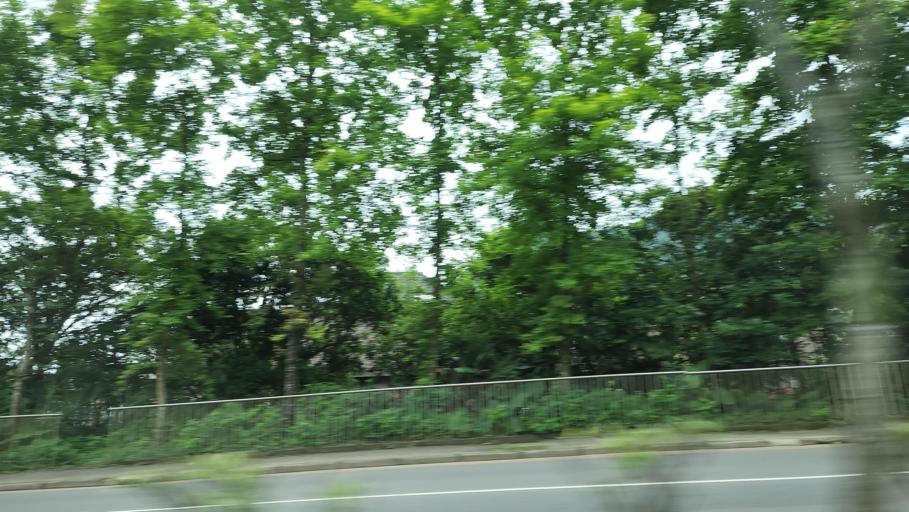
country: TW
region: Taiwan
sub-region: Keelung
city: Keelung
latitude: 25.1612
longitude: 121.6921
